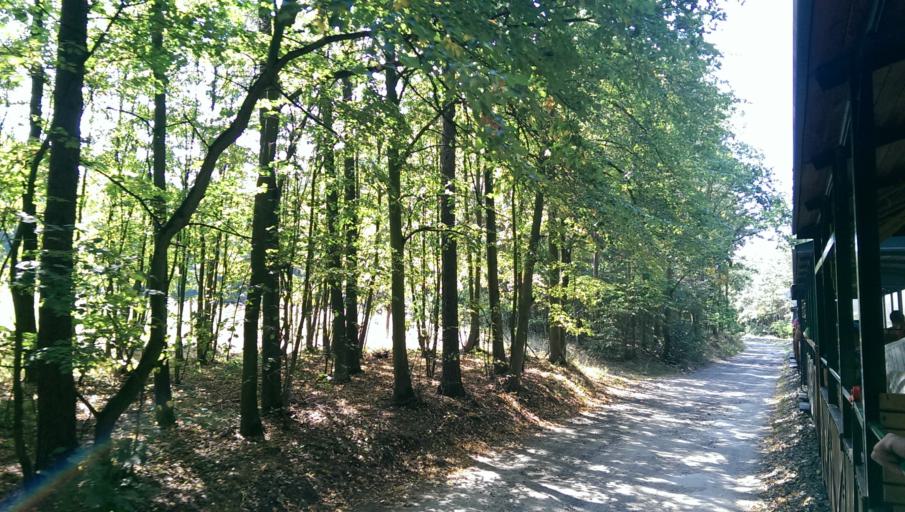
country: CZ
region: Central Bohemia
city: Stary Kolin
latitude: 50.0601
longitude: 15.2703
